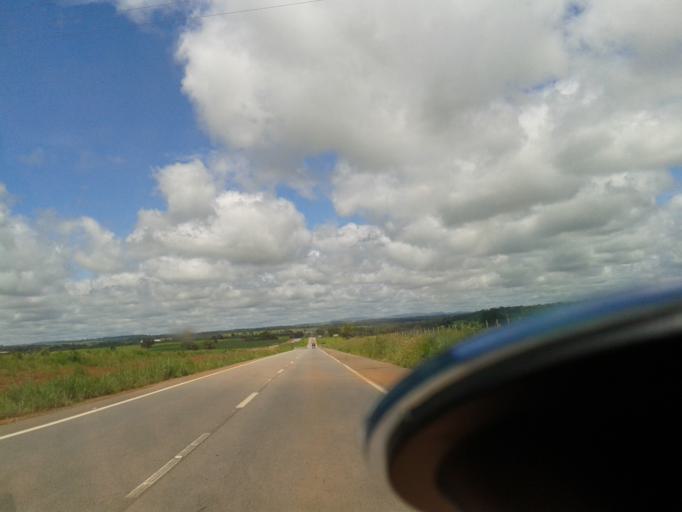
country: BR
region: Goias
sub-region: Itaberai
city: Itaberai
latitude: -16.1135
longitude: -49.6706
